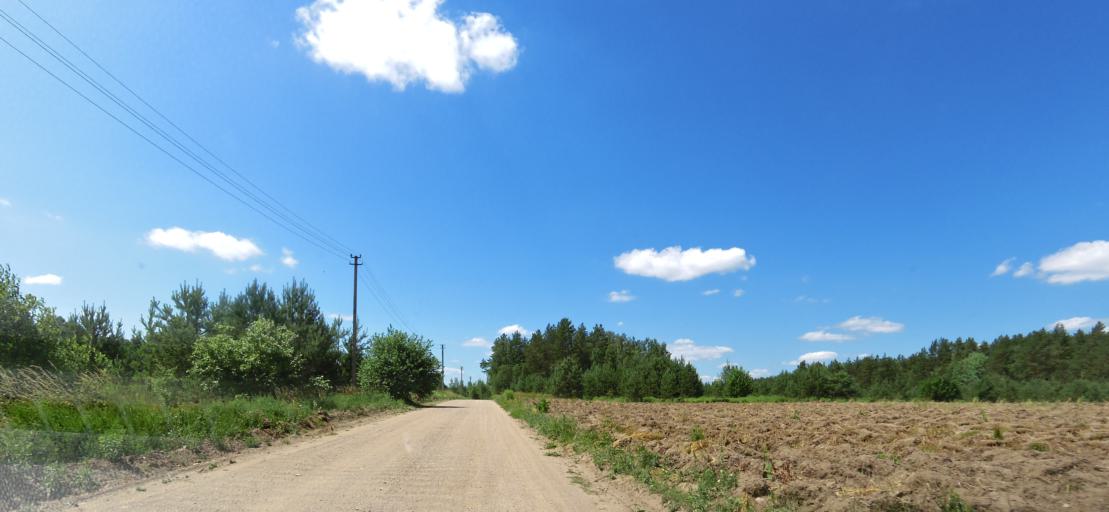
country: LT
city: Nemencine
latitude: 54.8717
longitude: 25.5587
